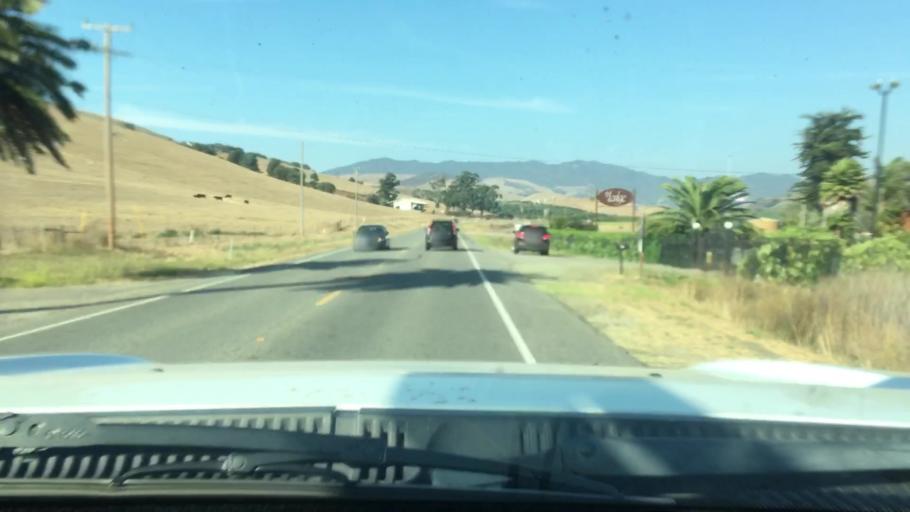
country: US
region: California
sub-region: San Luis Obispo County
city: Morro Bay
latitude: 35.3926
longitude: -120.8367
